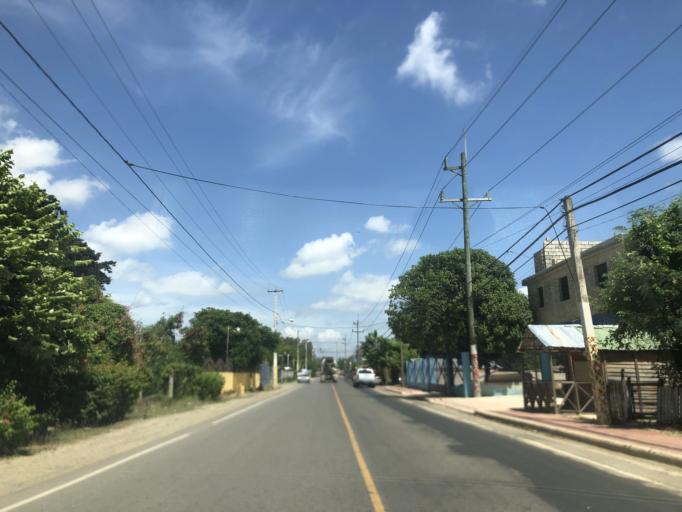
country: DO
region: Santiago
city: La Canela
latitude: 19.4507
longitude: -70.7738
